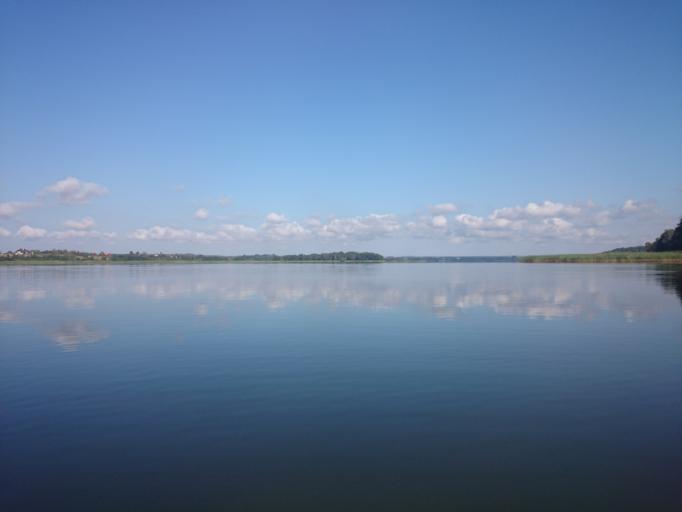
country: PL
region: Warmian-Masurian Voivodeship
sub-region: Powiat ostrodzki
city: Dabrowno
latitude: 53.4213
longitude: 20.0703
